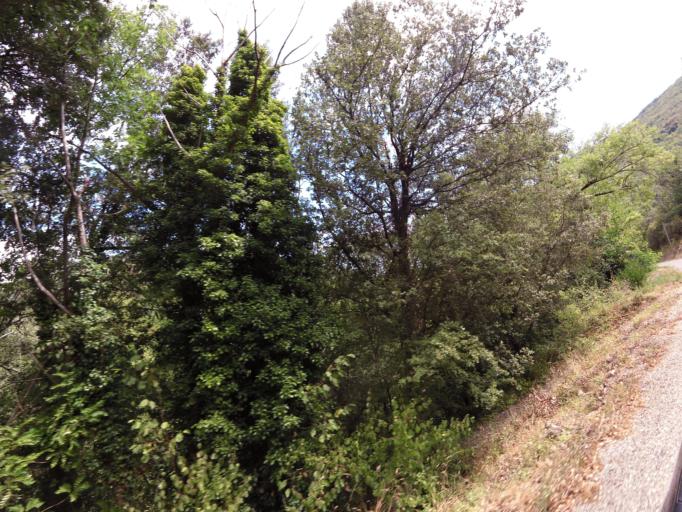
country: FR
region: Languedoc-Roussillon
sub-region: Departement du Gard
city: Le Vigan
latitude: 44.0021
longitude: 3.6582
